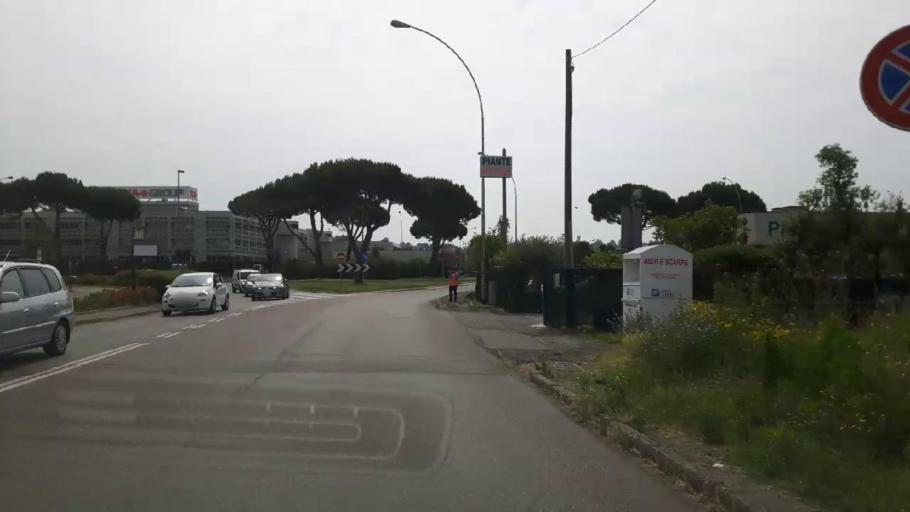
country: IT
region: Lombardy
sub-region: Provincia di Como
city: Grandate
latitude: 45.7682
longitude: 9.0582
